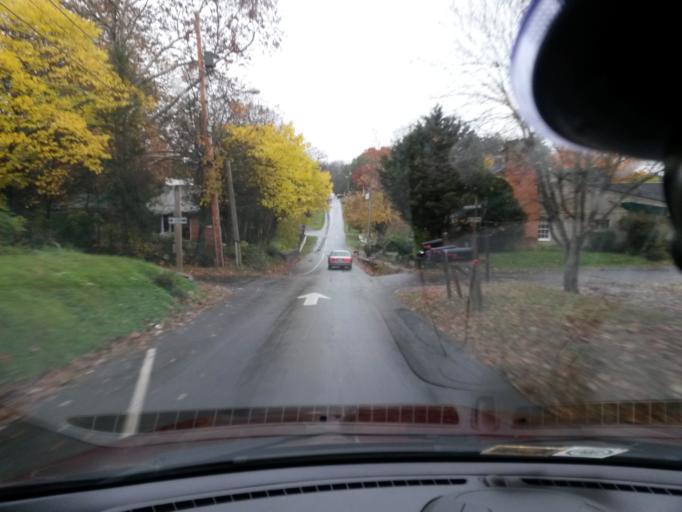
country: US
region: Virginia
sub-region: Botetourt County
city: Fincastle
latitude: 37.5001
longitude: -79.8735
